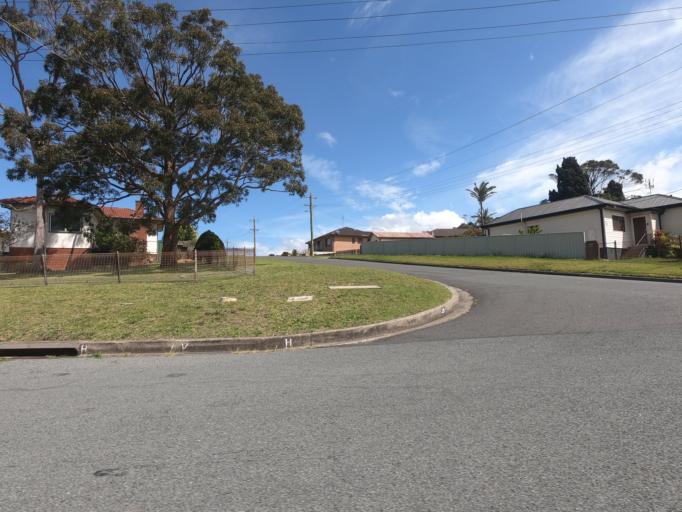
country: AU
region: New South Wales
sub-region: Wollongong
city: Lake Heights
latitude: -34.4880
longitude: 150.8703
